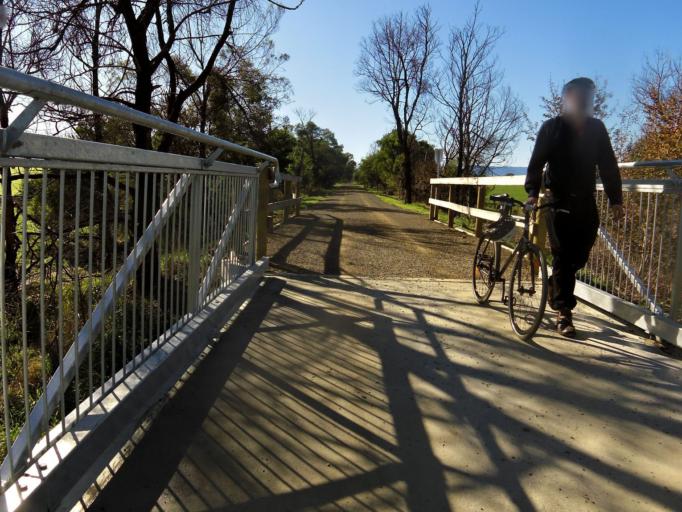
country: AU
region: Victoria
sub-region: Yarra Ranges
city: Lilydale
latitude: -37.7331
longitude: 145.3686
